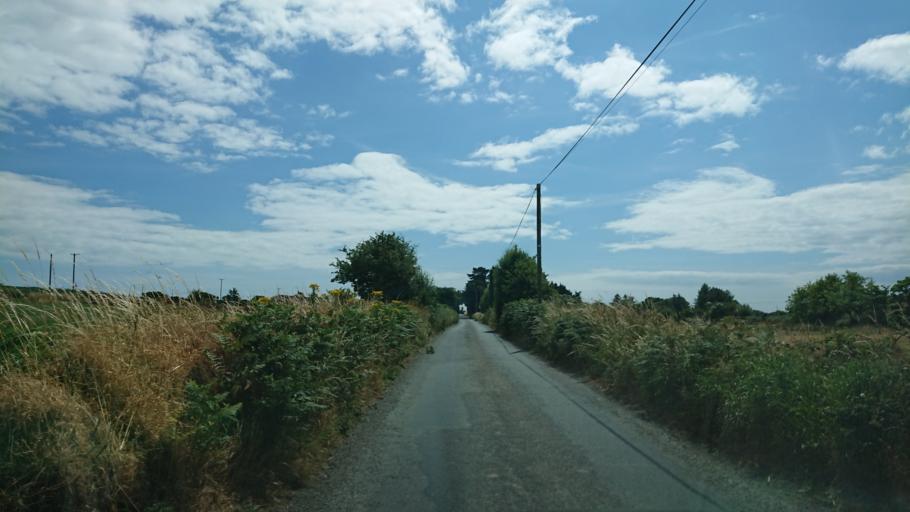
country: IE
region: Munster
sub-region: Waterford
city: Portlaw
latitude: 52.2021
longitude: -7.3288
